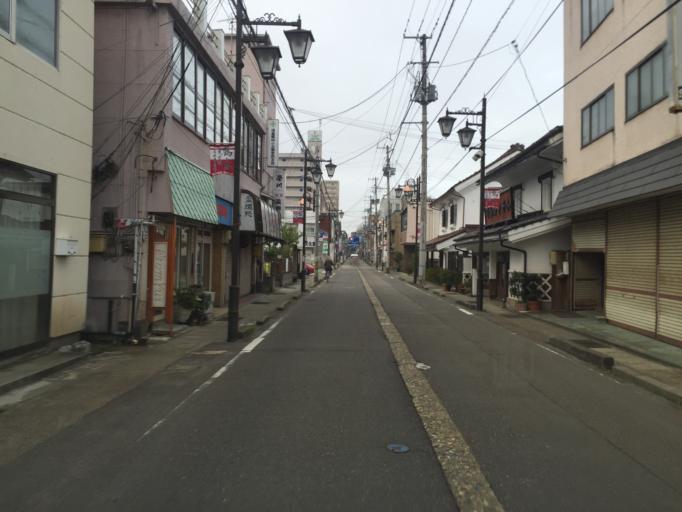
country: JP
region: Fukushima
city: Kitakata
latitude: 37.5019
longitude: 139.9290
